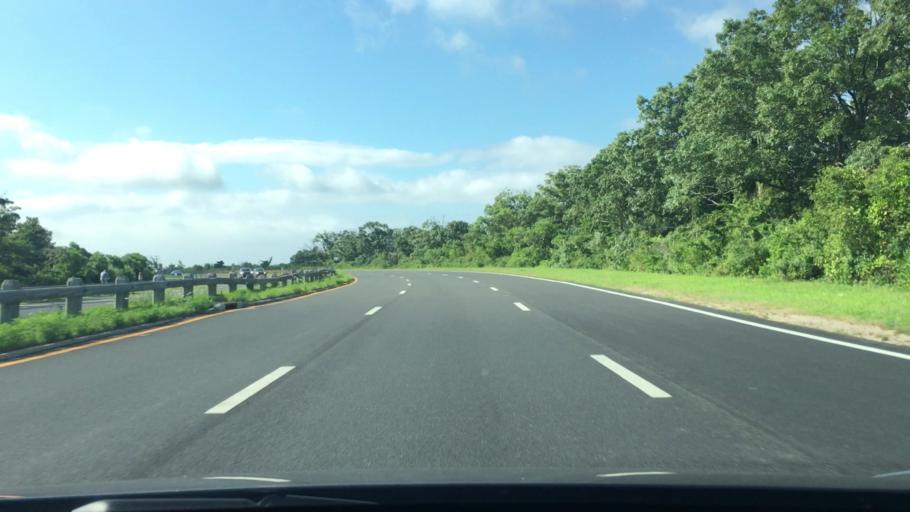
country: US
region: New York
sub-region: Nassau County
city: Bellmore
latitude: 40.6444
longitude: -73.5101
